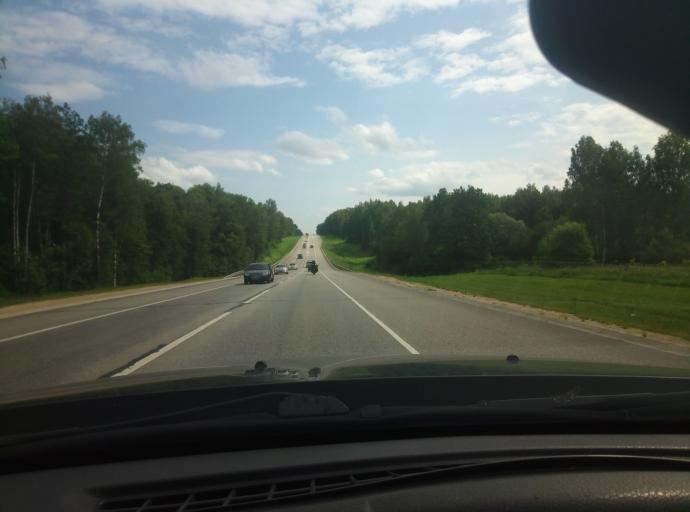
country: RU
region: Tula
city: Leninskiy
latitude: 54.3860
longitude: 37.5128
